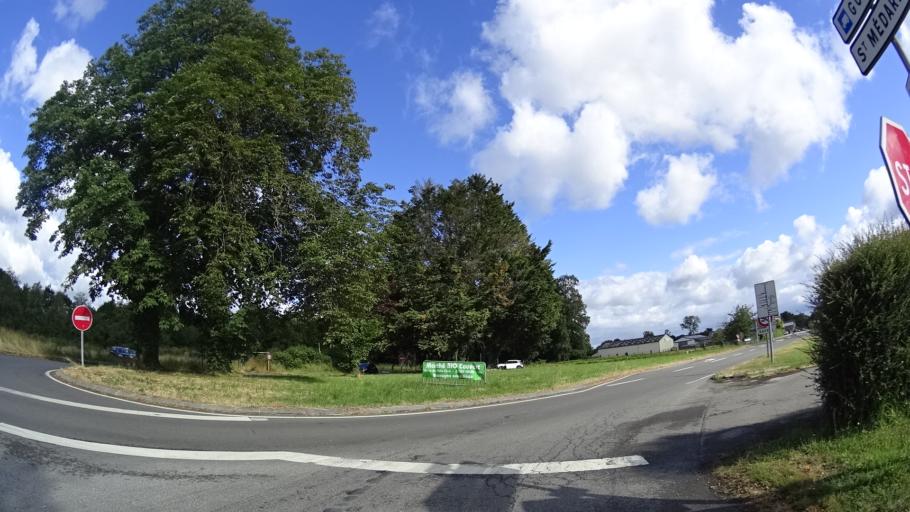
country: FR
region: Brittany
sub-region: Departement d'Ille-et-Vilaine
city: Hede-Bazouges
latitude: 48.2860
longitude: -1.8011
